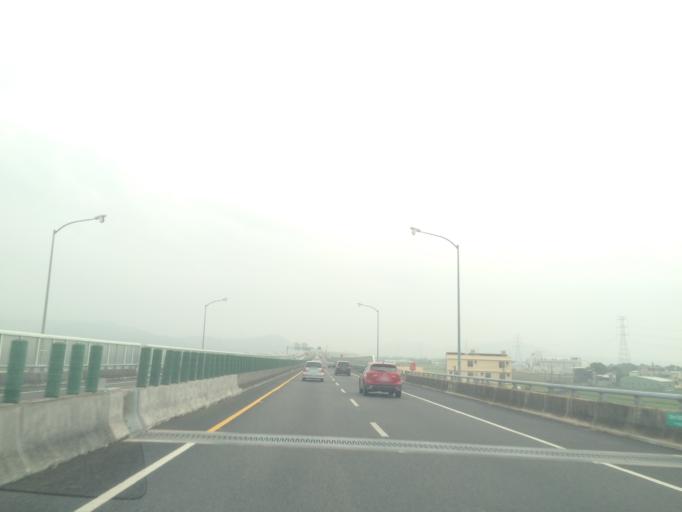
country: TW
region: Taiwan
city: Zhongxing New Village
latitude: 24.0256
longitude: 120.6718
